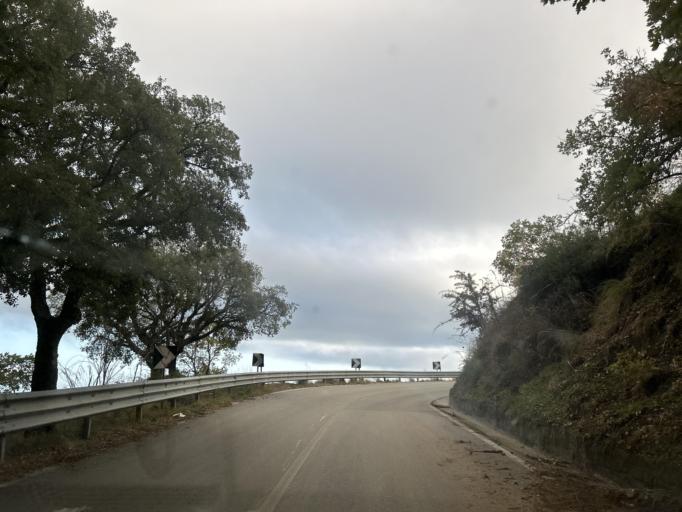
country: IT
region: Calabria
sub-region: Provincia di Catanzaro
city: Squillace Lido
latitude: 38.7597
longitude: 16.5650
